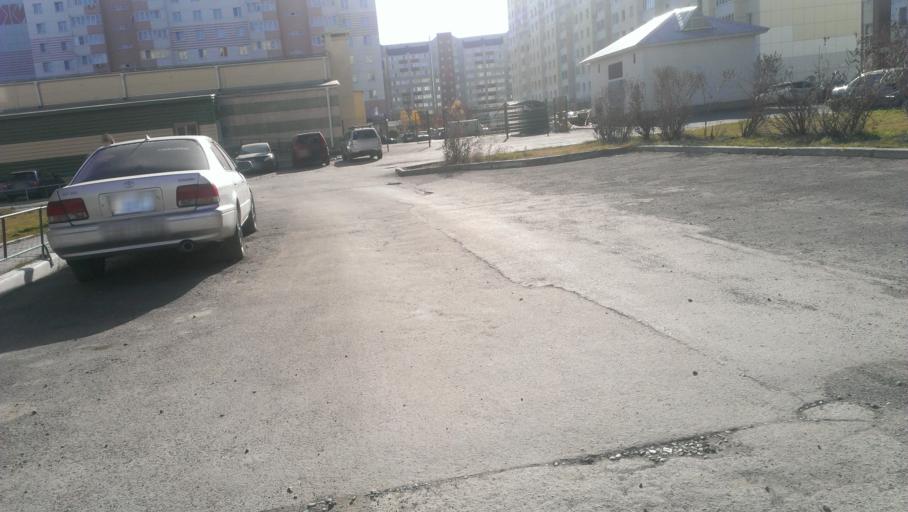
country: RU
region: Altai Krai
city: Novosilikatnyy
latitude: 53.3370
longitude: 83.6925
